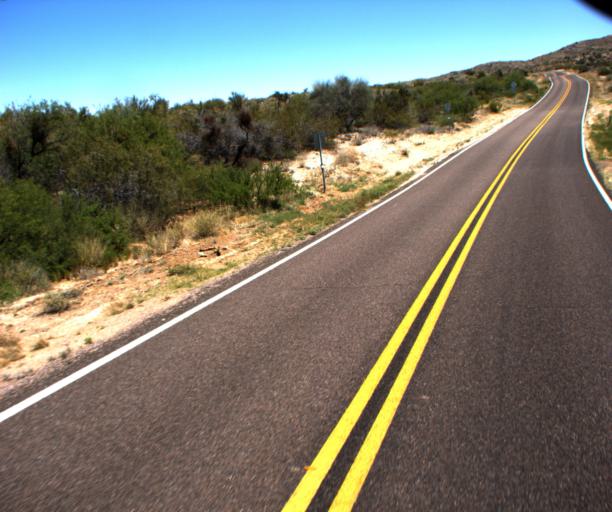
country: US
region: Arizona
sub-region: Yavapai County
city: Bagdad
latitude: 34.5020
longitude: -113.1641
